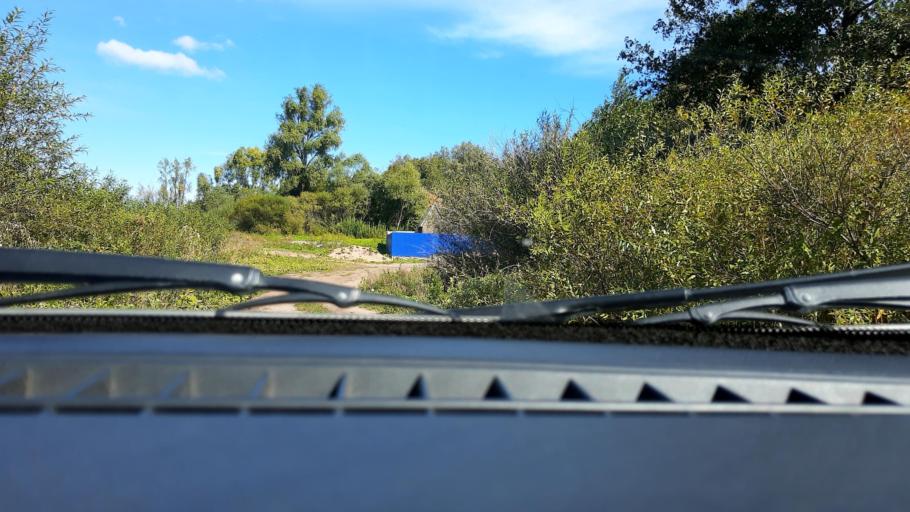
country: RU
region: Bashkortostan
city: Mikhaylovka
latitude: 54.8201
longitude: 55.7894
